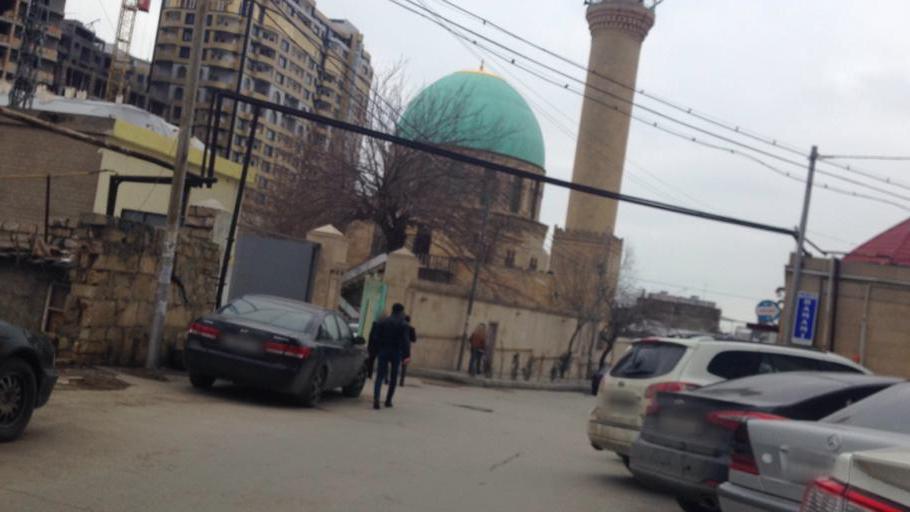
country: AZ
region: Baki
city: Badamdar
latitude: 40.3793
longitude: 49.8290
